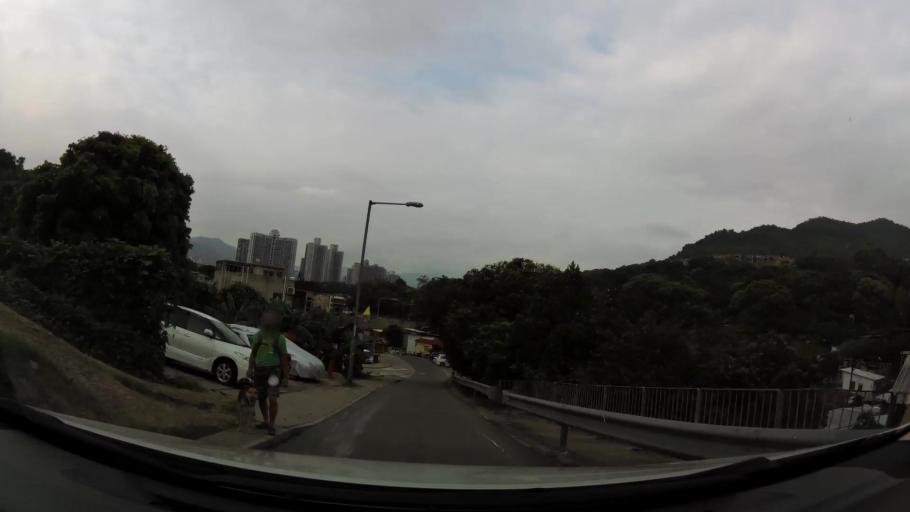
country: HK
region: Tai Po
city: Tai Po
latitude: 22.4350
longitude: 114.1640
